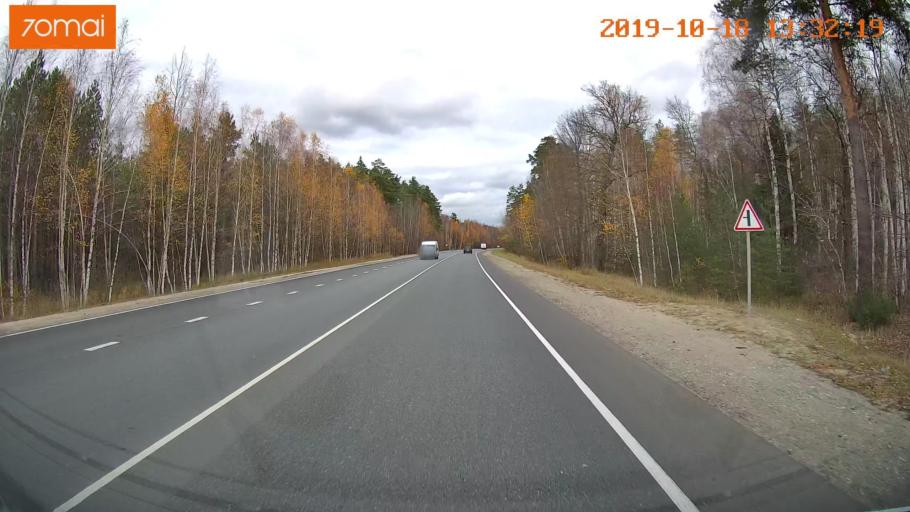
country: RU
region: Rjazan
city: Solotcha
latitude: 54.8315
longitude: 39.9168
